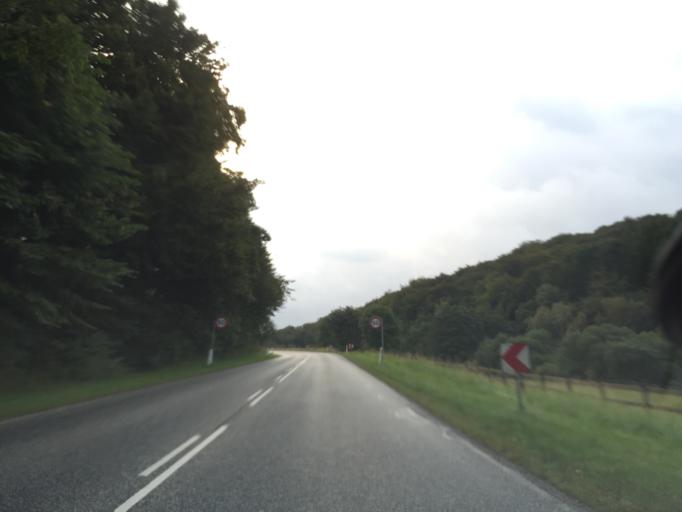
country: DK
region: Central Jutland
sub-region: Skanderborg Kommune
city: Galten
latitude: 56.1213
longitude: 9.8592
